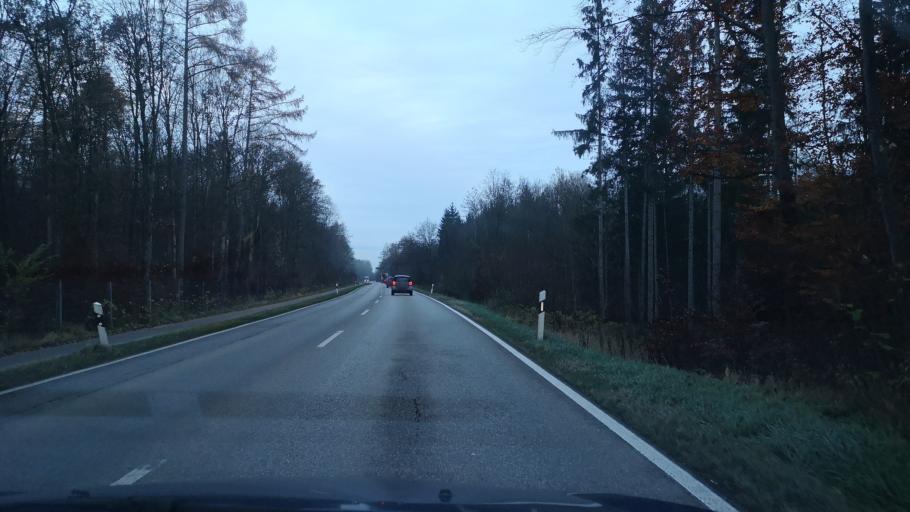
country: DE
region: Bavaria
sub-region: Upper Bavaria
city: Forstinning
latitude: 48.1522
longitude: 11.9116
